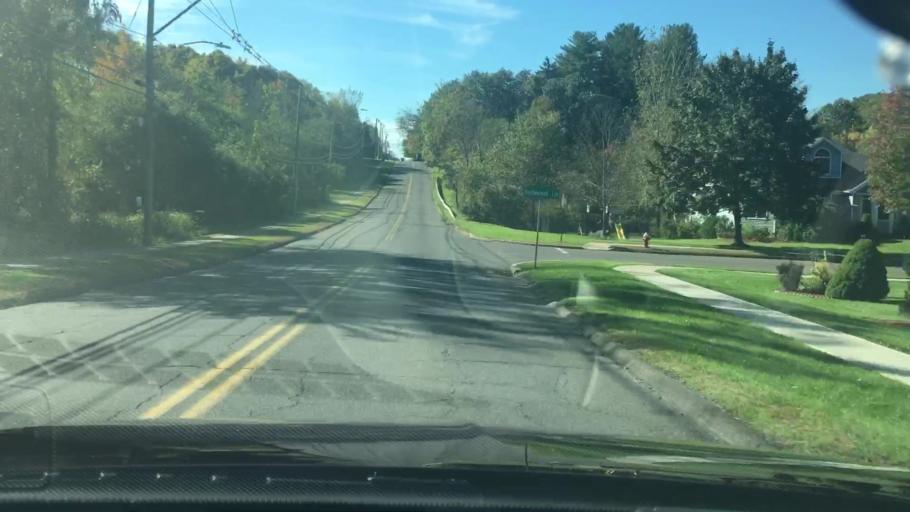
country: US
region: Connecticut
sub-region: Hartford County
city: Kensington
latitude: 41.6178
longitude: -72.7206
